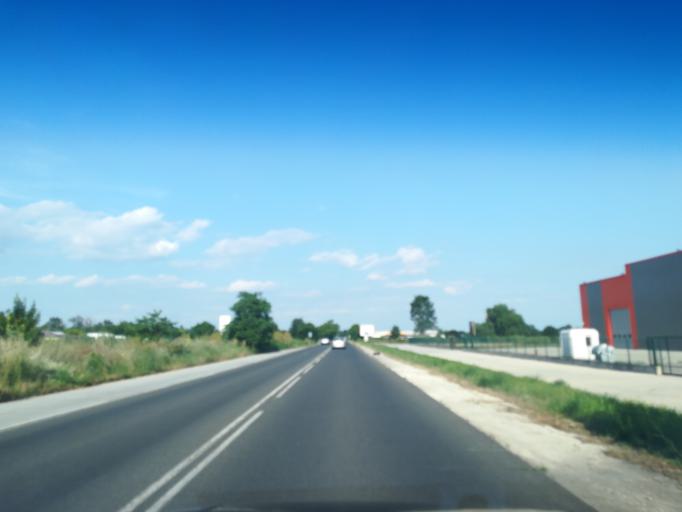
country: BG
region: Plovdiv
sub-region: Obshtina Plovdiv
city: Plovdiv
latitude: 42.1492
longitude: 24.8219
